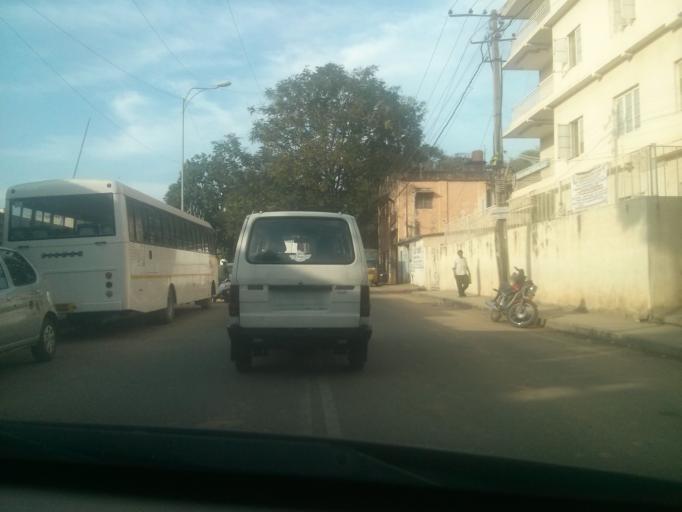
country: IN
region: Karnataka
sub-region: Bangalore Urban
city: Bangalore
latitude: 12.9540
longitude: 77.5722
